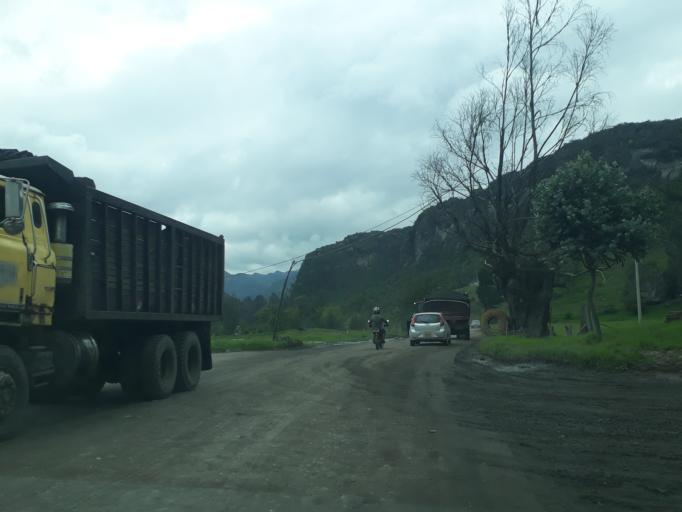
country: CO
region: Cundinamarca
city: Lenguazaque
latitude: 5.3277
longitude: -73.7065
